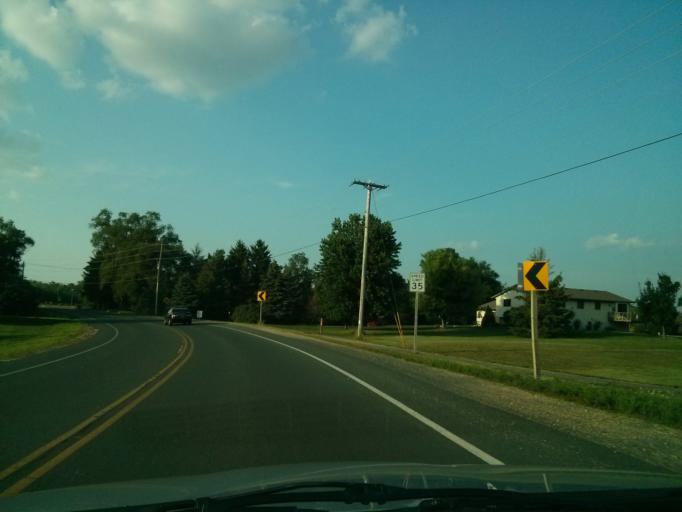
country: US
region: Wisconsin
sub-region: Saint Croix County
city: North Hudson
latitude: 44.9884
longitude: -92.7061
